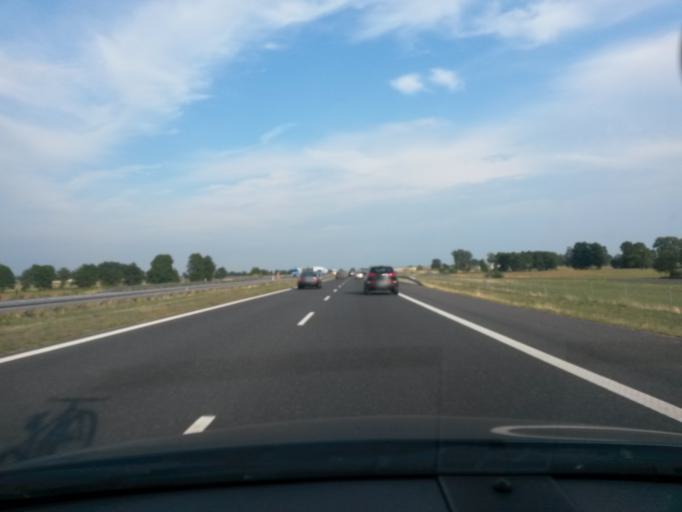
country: PL
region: Lodz Voivodeship
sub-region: Powiat poddebicki
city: Dalikow
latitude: 51.9661
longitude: 19.1084
